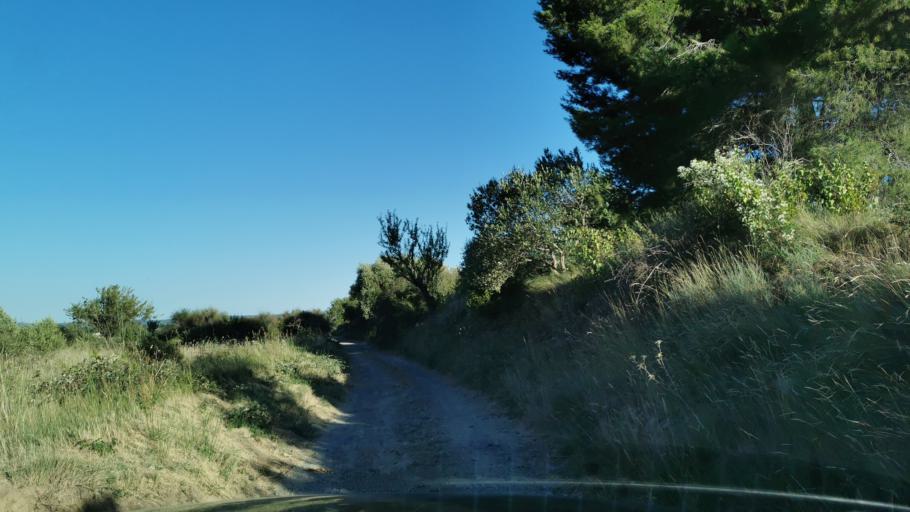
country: FR
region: Languedoc-Roussillon
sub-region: Departement de l'Aude
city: Ouveillan
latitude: 43.2698
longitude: 2.9794
